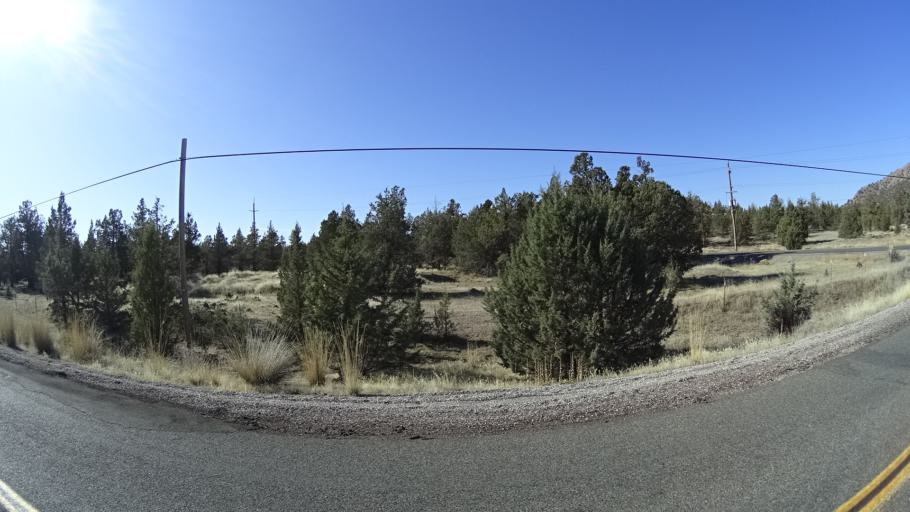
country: US
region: California
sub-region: Siskiyou County
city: Montague
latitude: 41.6613
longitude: -122.3680
